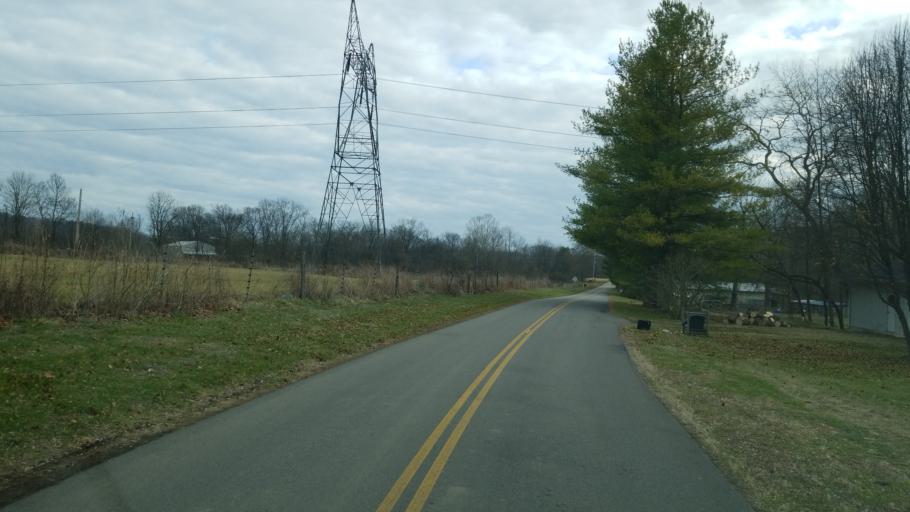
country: US
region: Ohio
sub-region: Highland County
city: Greenfield
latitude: 39.2356
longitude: -83.3346
